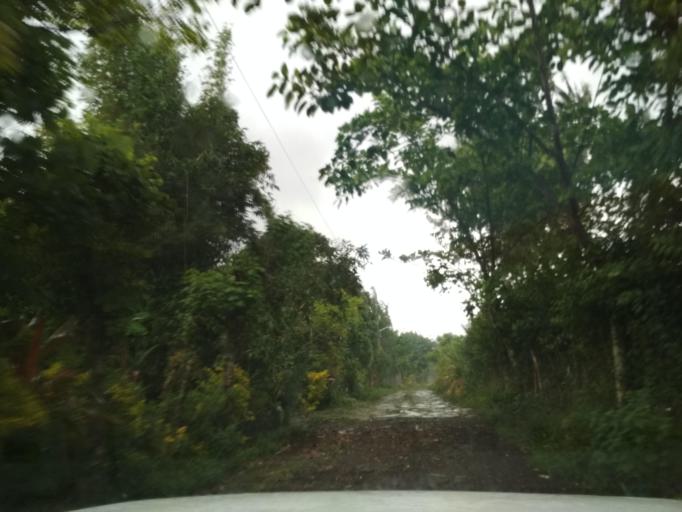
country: MX
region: Veracruz
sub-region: Mariano Escobedo
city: Chicola
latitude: 18.9057
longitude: -97.1174
